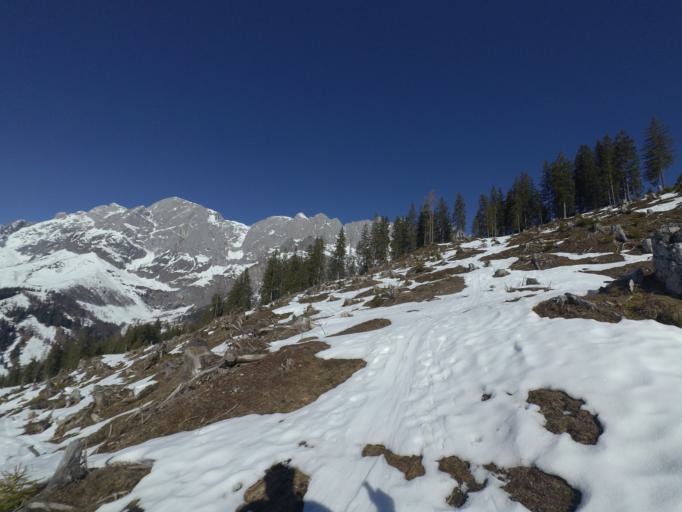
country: AT
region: Salzburg
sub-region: Politischer Bezirk Sankt Johann im Pongau
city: Muhlbach am Hochkonig
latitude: 47.3950
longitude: 13.1211
